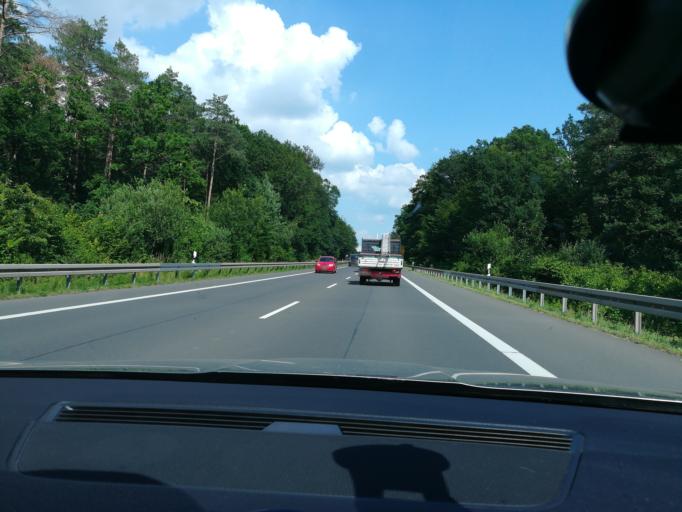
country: DE
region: North Rhine-Westphalia
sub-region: Regierungsbezirk Detmold
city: Petershagen
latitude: 52.3795
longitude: 8.9456
